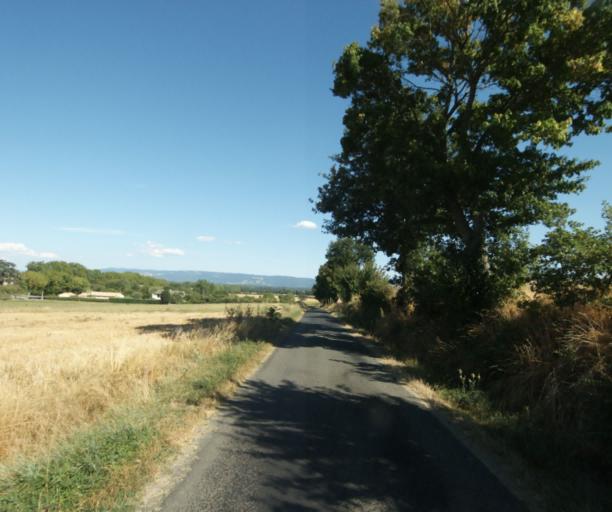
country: FR
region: Midi-Pyrenees
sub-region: Departement de la Haute-Garonne
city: Revel
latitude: 43.5034
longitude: 1.9448
